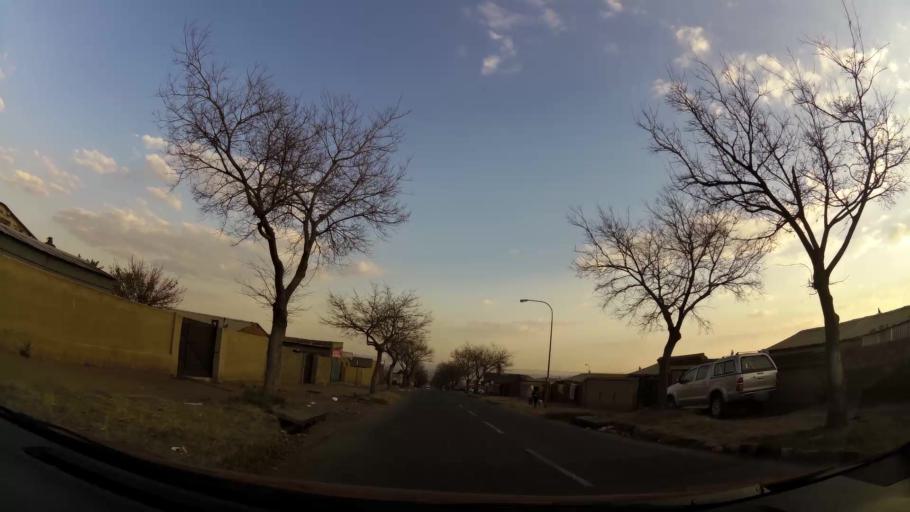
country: ZA
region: Gauteng
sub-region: City of Johannesburg Metropolitan Municipality
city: Roodepoort
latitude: -26.2178
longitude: 27.8929
